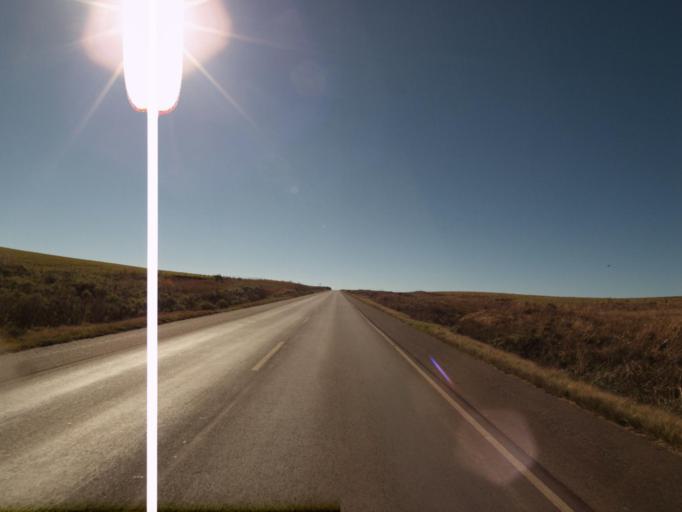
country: BR
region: Parana
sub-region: Palmas
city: Palmas
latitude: -26.7230
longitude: -51.6280
